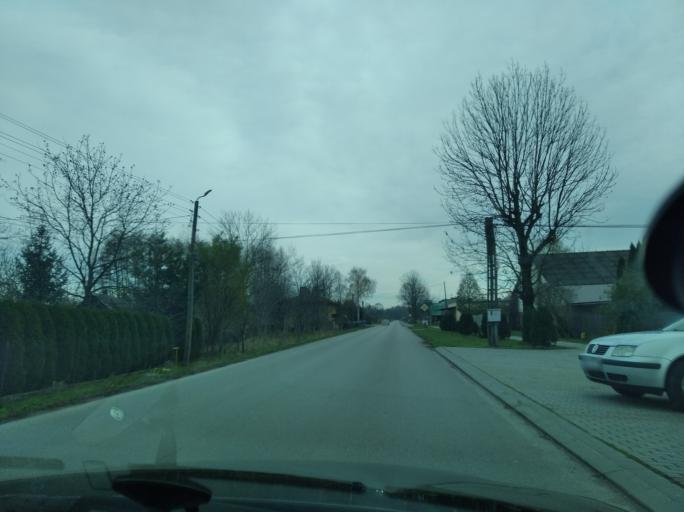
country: PL
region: Subcarpathian Voivodeship
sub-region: Powiat przeworski
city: Gac
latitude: 50.0284
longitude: 22.3713
